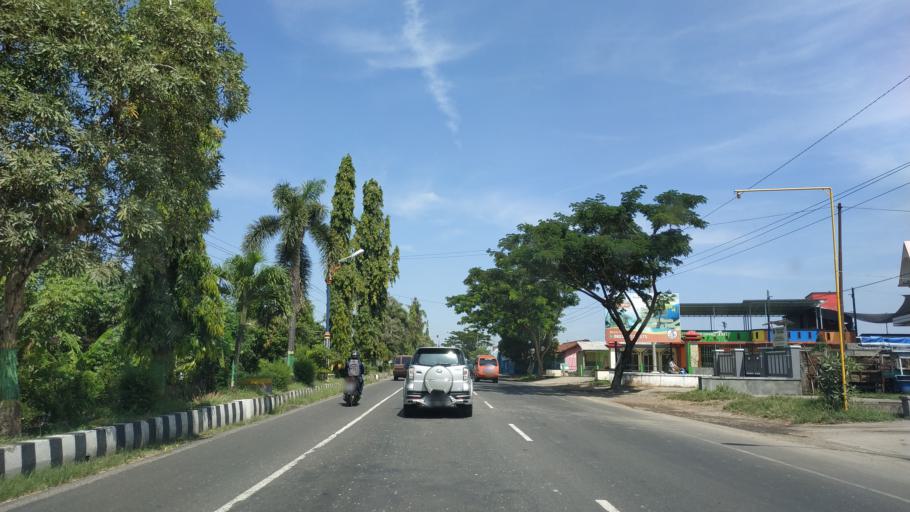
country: ID
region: Central Java
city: Geritan
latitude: -6.7490
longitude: 111.0598
